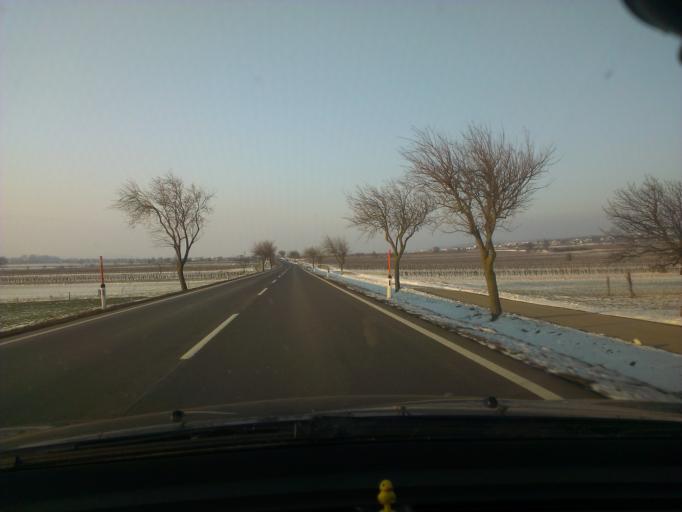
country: AT
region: Burgenland
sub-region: Eisenstadt-Umgebung
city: Breitenbrunn
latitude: 47.9296
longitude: 16.7166
